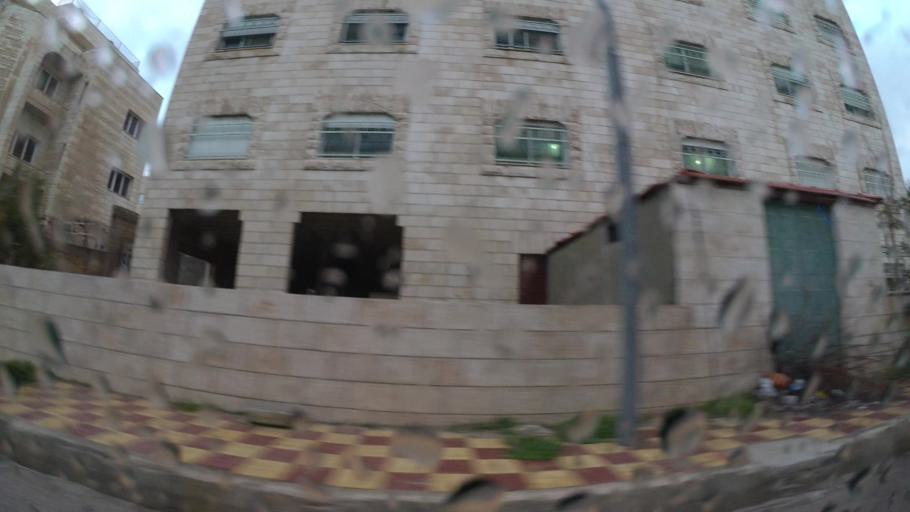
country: JO
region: Amman
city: Amman
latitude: 31.9953
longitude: 35.9211
